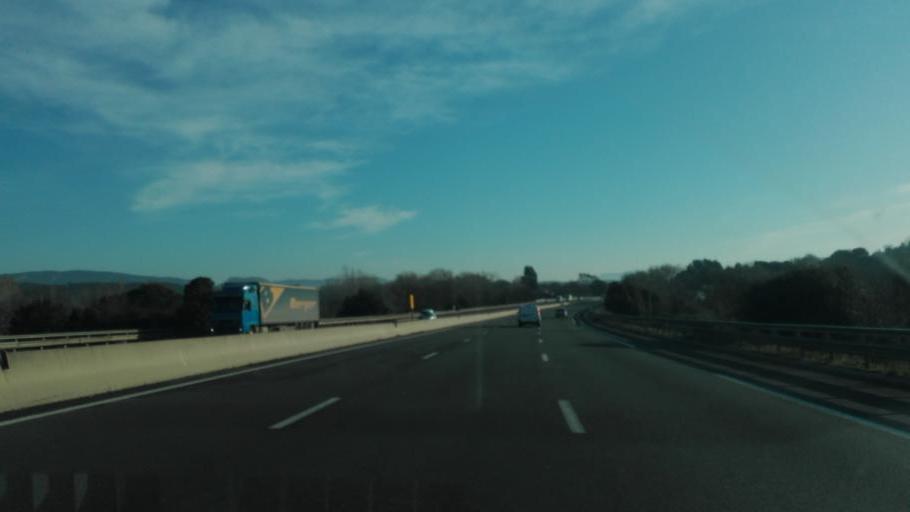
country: FR
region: Provence-Alpes-Cote d'Azur
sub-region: Departement du Var
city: Le Muy
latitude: 43.4636
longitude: 6.5641
